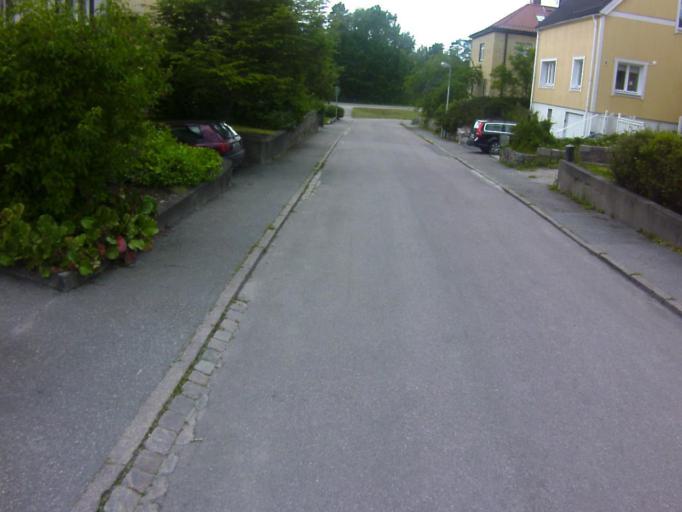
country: SE
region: Soedermanland
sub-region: Eskilstuna Kommun
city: Eskilstuna
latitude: 59.3641
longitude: 16.4994
